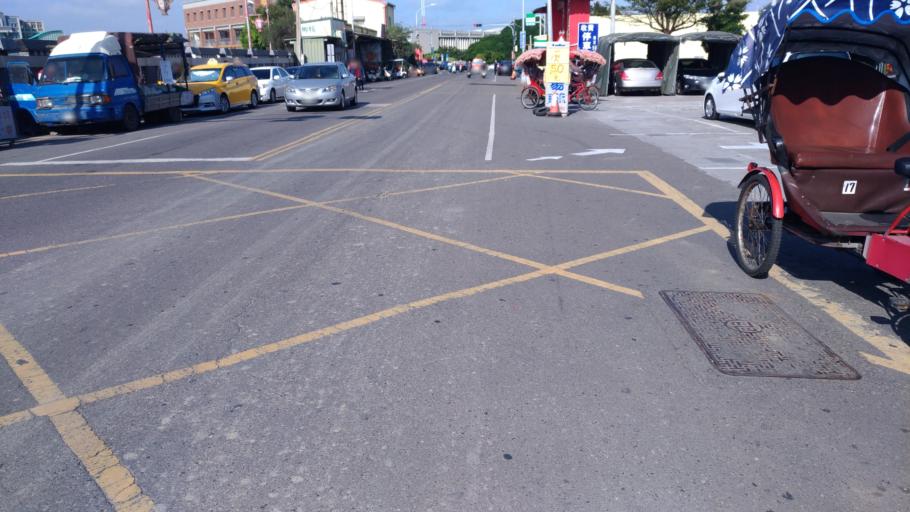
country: TW
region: Taiwan
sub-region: Changhua
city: Chang-hua
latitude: 24.0567
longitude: 120.4284
